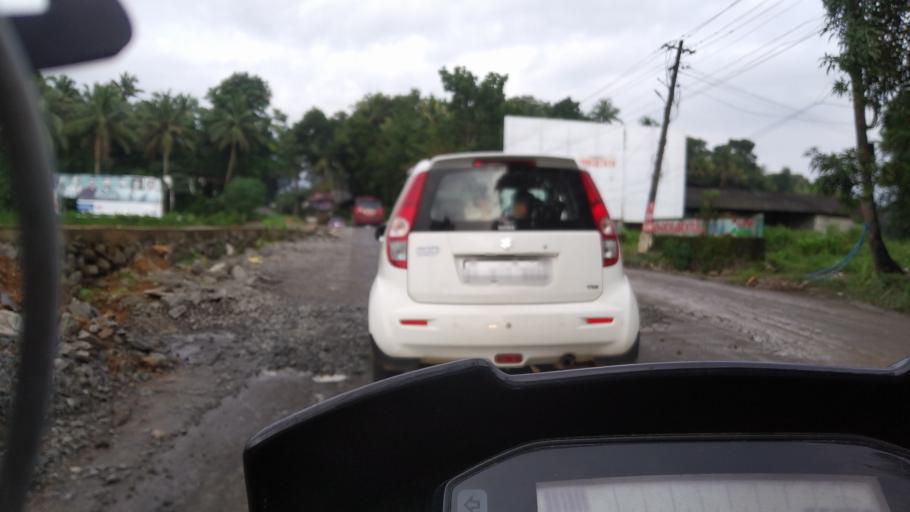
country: IN
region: Kerala
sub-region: Idukki
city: Kuttampuzha
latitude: 10.0503
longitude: 76.7315
